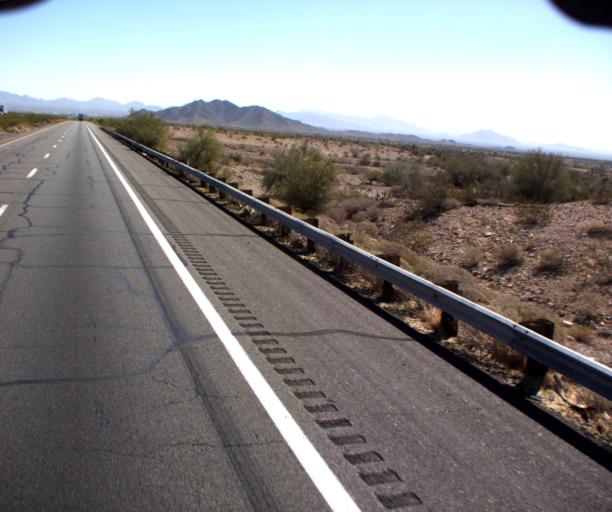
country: US
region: Arizona
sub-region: La Paz County
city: Quartzsite
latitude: 33.6494
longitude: -114.3119
